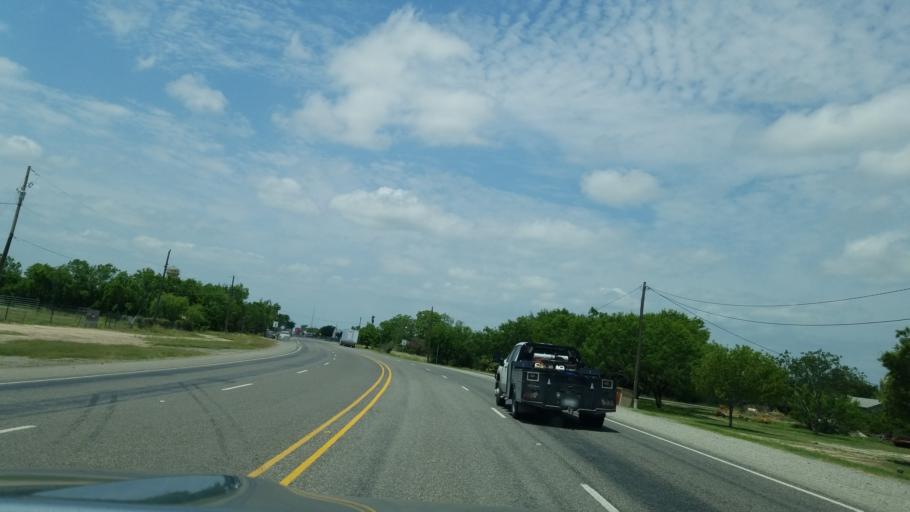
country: US
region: Texas
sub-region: Zavala County
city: La Pryor
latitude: 28.9459
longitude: -99.8360
